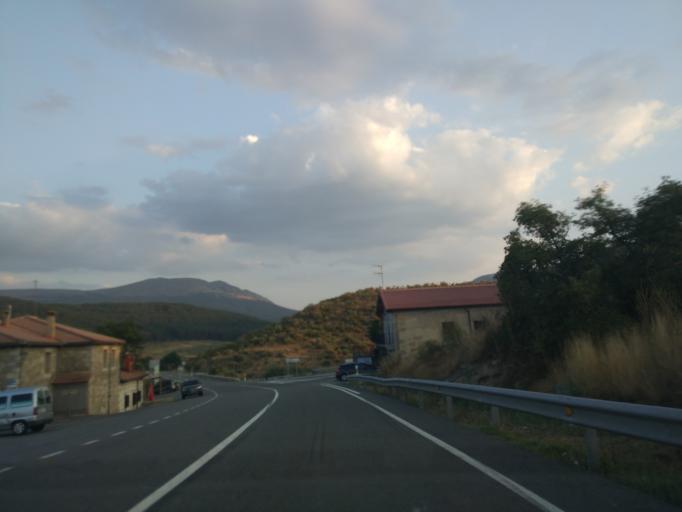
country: ES
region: Castille and Leon
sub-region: Provincia de Avila
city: San Martin del Pimpollar
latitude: 40.3740
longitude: -5.0181
